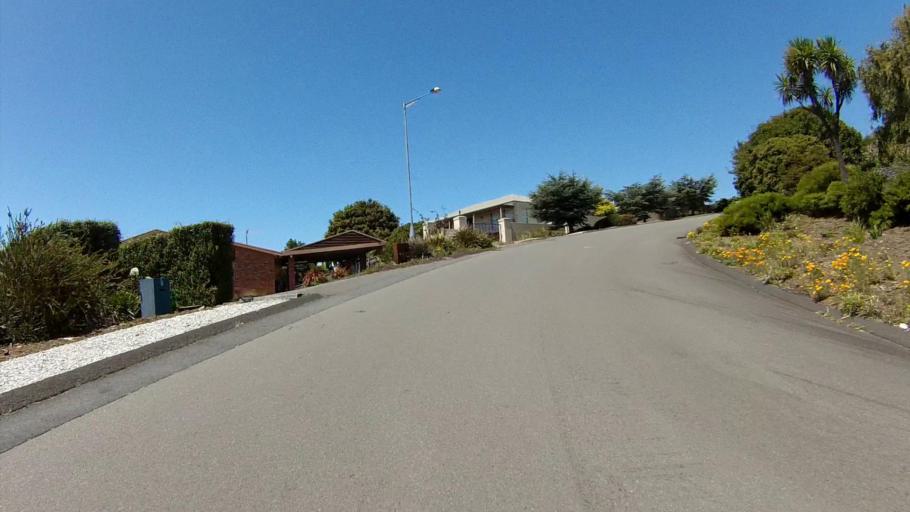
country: AU
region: Tasmania
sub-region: Clarence
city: Sandford
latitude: -42.9169
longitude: 147.5110
